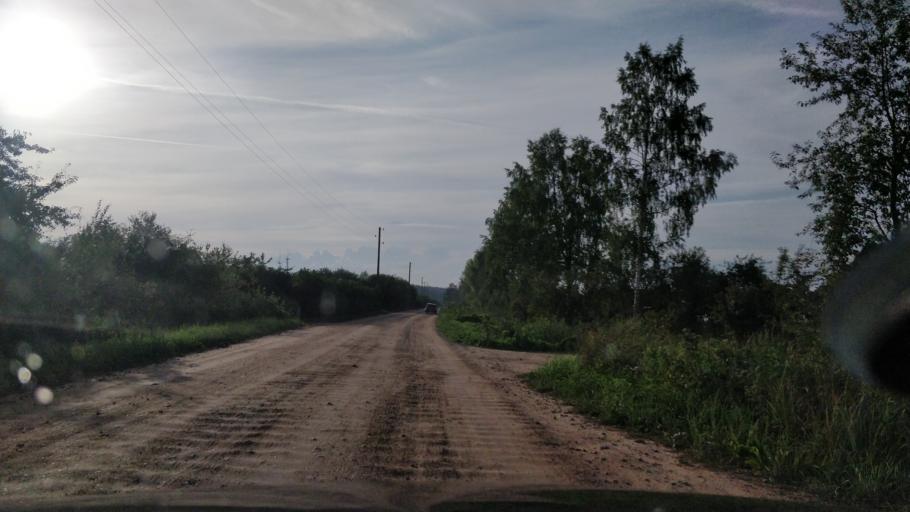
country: LV
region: Incukalns
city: Incukalns
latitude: 57.0969
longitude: 24.7577
